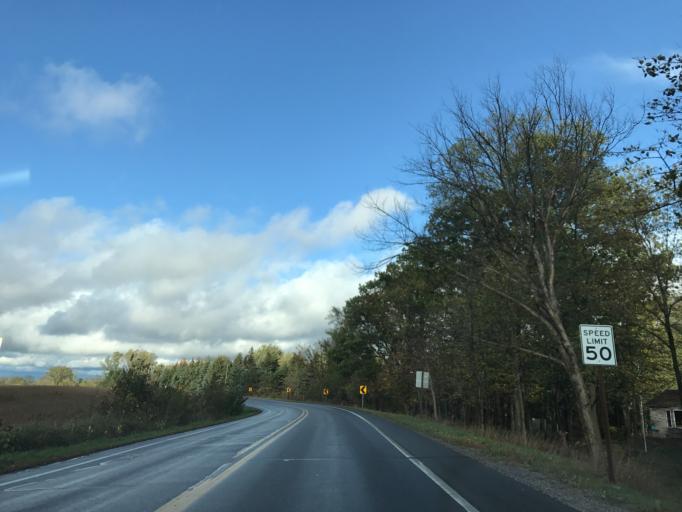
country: US
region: Michigan
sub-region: Oakland County
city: South Lyon
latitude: 42.3816
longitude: -83.6455
